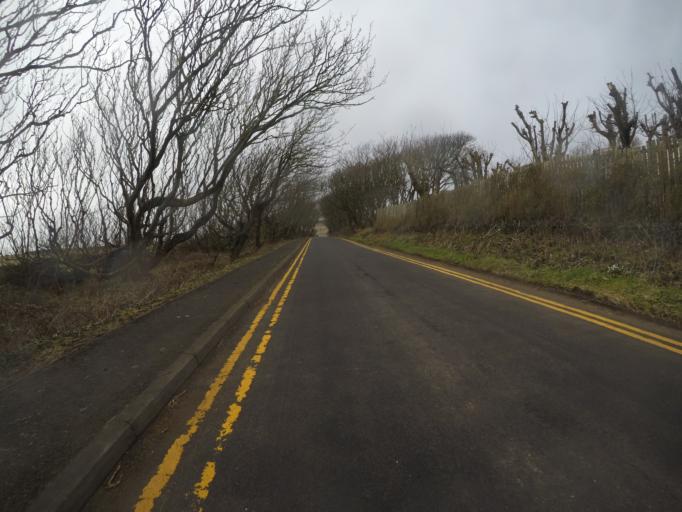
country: GB
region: Scotland
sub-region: North Ayrshire
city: West Kilbride
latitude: 55.6973
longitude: -4.8890
